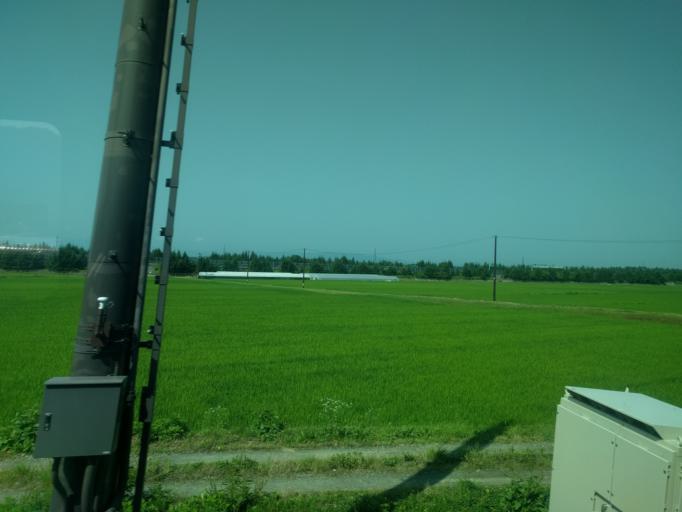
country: JP
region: Fukushima
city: Inawashiro
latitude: 37.5330
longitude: 140.1391
